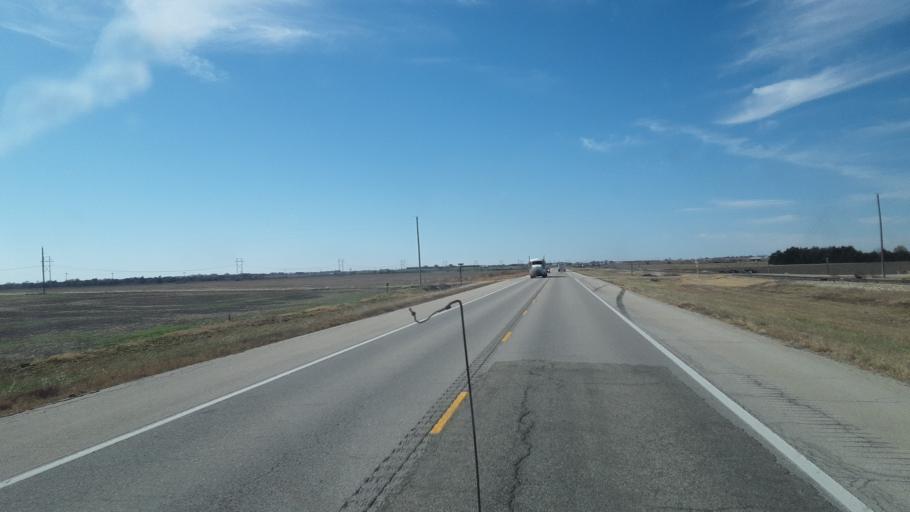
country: US
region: Kansas
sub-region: McPherson County
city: McPherson
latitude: 38.3662
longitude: -97.7390
